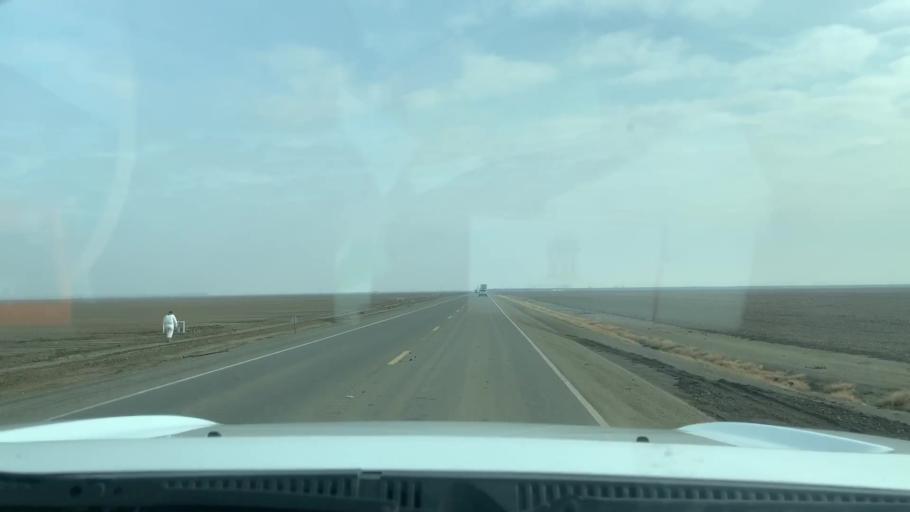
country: US
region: California
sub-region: Kings County
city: Lemoore Station
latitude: 36.2554
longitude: -119.9944
